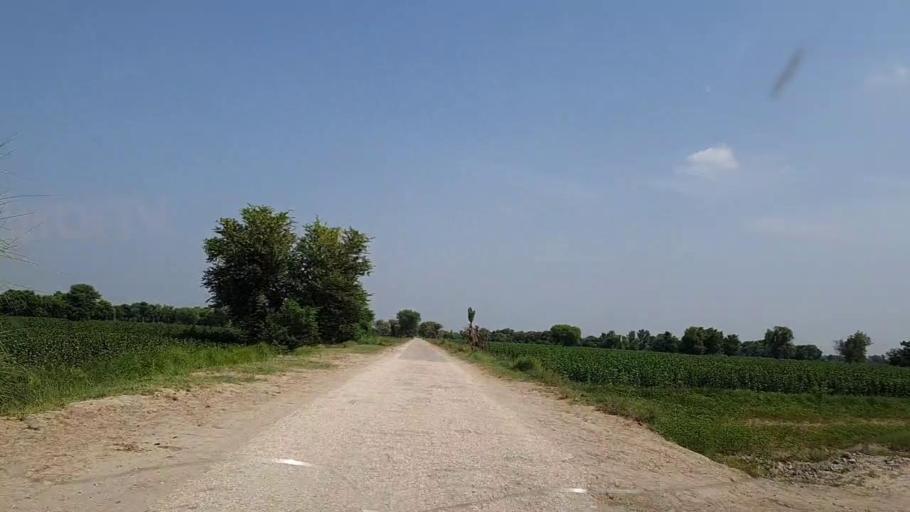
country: PK
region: Sindh
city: Adilpur
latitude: 27.8318
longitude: 69.2899
